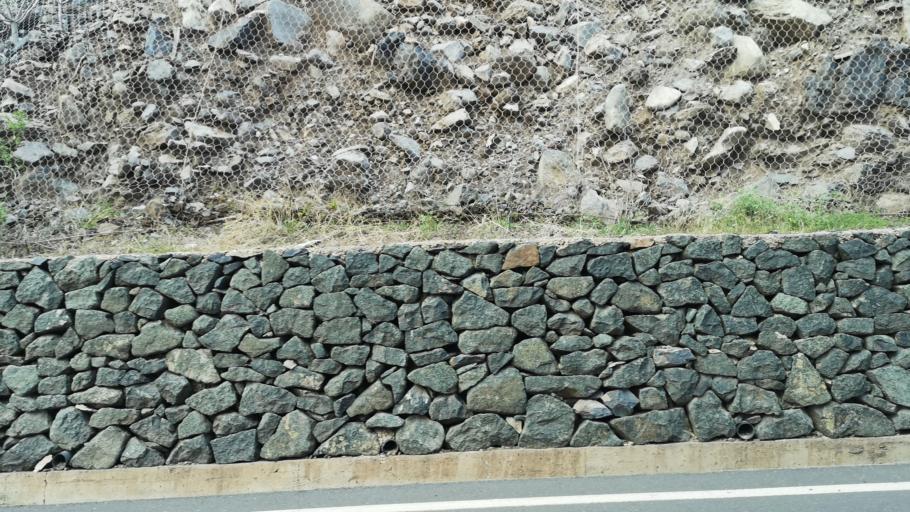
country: ES
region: Canary Islands
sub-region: Provincia de Santa Cruz de Tenerife
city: Hermigua
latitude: 28.1797
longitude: -17.1862
